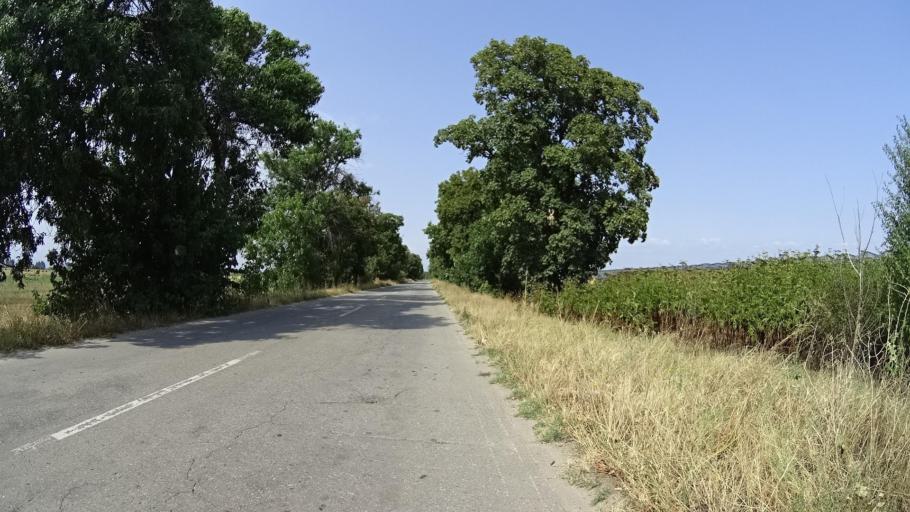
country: BG
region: Plovdiv
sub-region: Obshtina Kaloyanovo
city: Kaloyanovo
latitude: 42.2587
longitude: 24.7999
